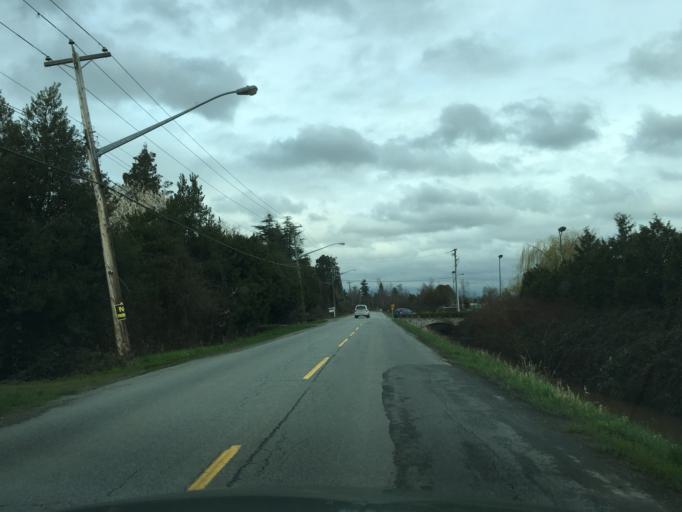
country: CA
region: British Columbia
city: Richmond
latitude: 49.1593
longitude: -123.0689
